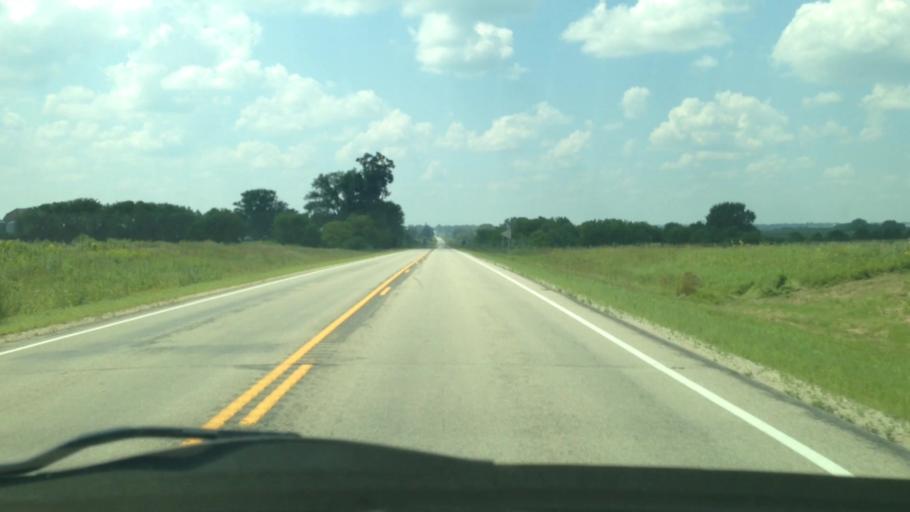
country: US
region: Minnesota
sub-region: Olmsted County
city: Stewartville
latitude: 43.8554
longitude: -92.4280
